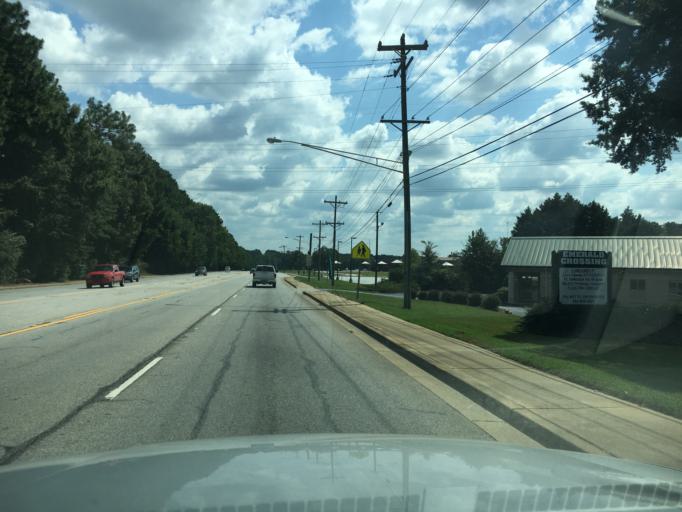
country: US
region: South Carolina
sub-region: Greenwood County
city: Greenwood
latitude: 34.1939
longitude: -82.1884
